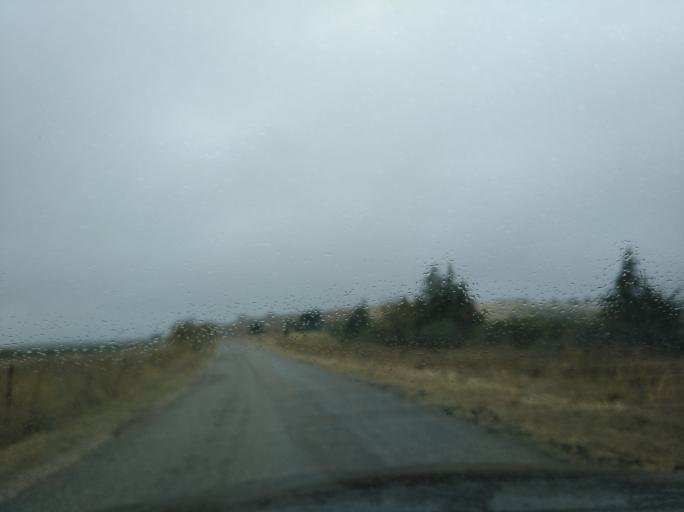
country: PT
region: Portalegre
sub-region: Campo Maior
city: Campo Maior
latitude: 38.9818
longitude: -7.0915
